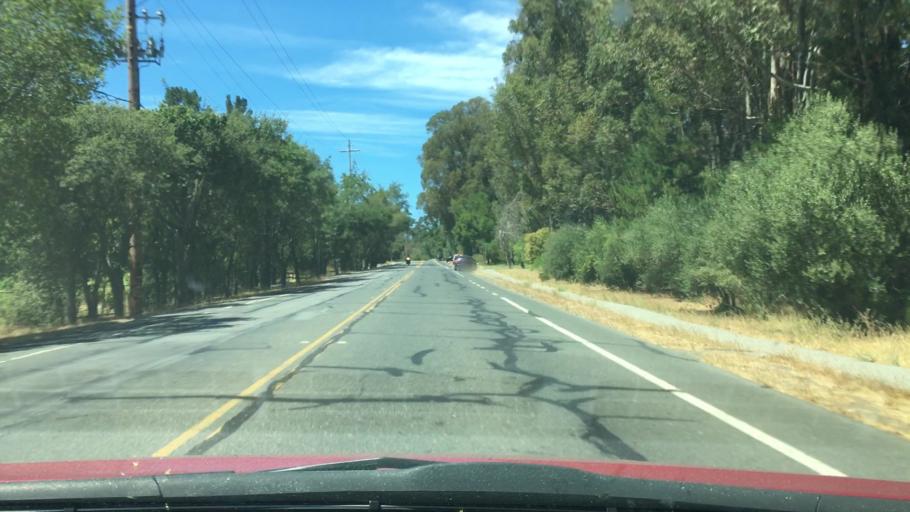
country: US
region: California
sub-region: San Mateo County
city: Woodside
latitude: 37.4412
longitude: -122.2658
